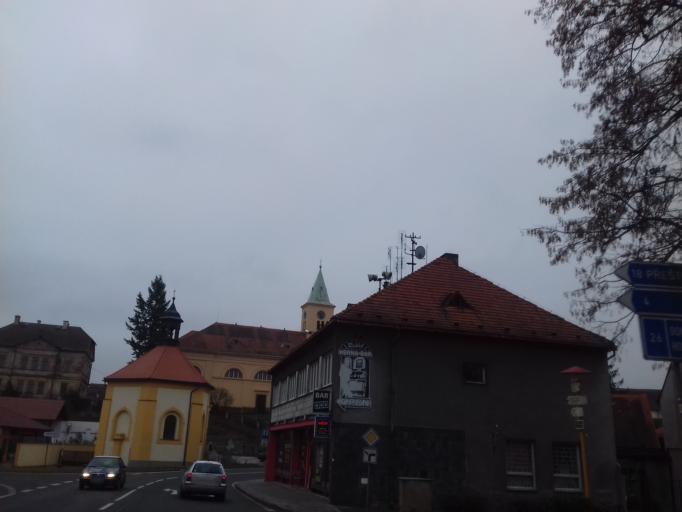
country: CZ
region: Plzensky
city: Stod
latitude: 49.6378
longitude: 13.1659
